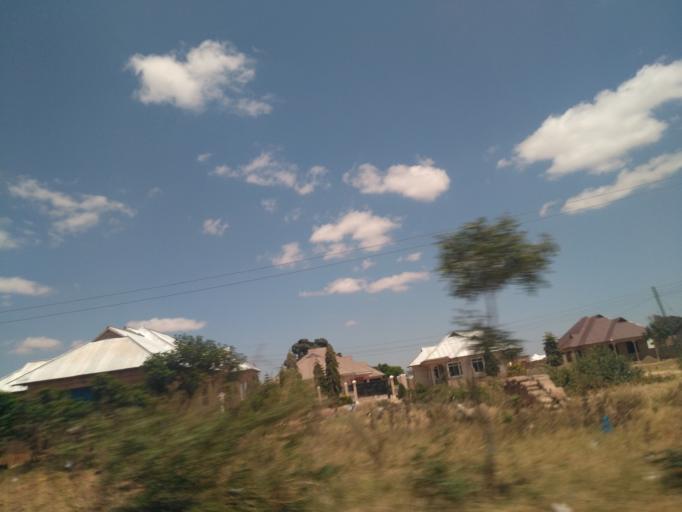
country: TZ
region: Dodoma
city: Kisasa
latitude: -6.1700
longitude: 35.7912
